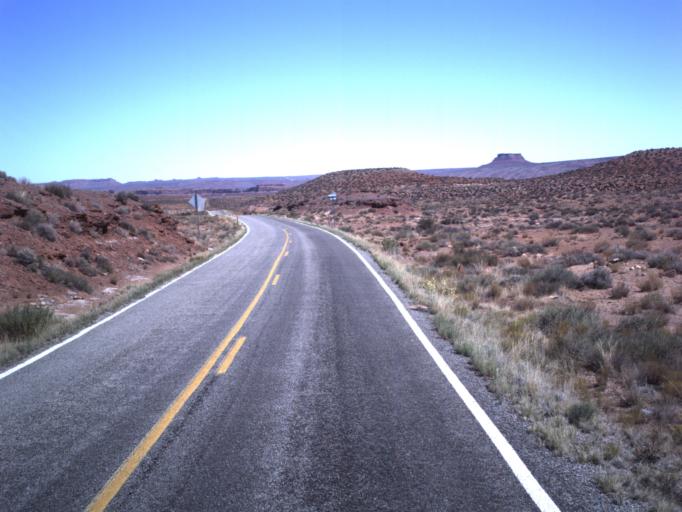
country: US
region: Arizona
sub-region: Navajo County
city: Kayenta
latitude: 37.1947
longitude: -109.9080
